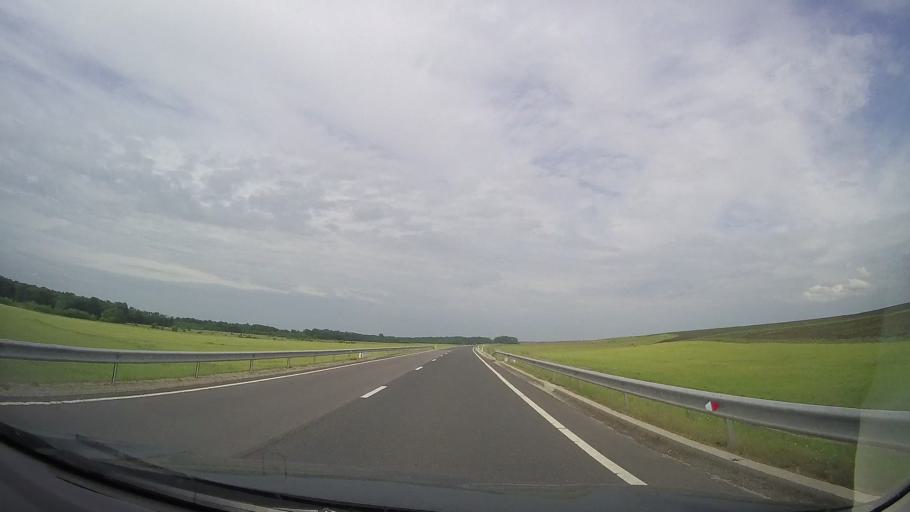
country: RO
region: Teleorman
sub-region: Comuna Nanov
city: Nanov
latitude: 44.0081
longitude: 25.2858
